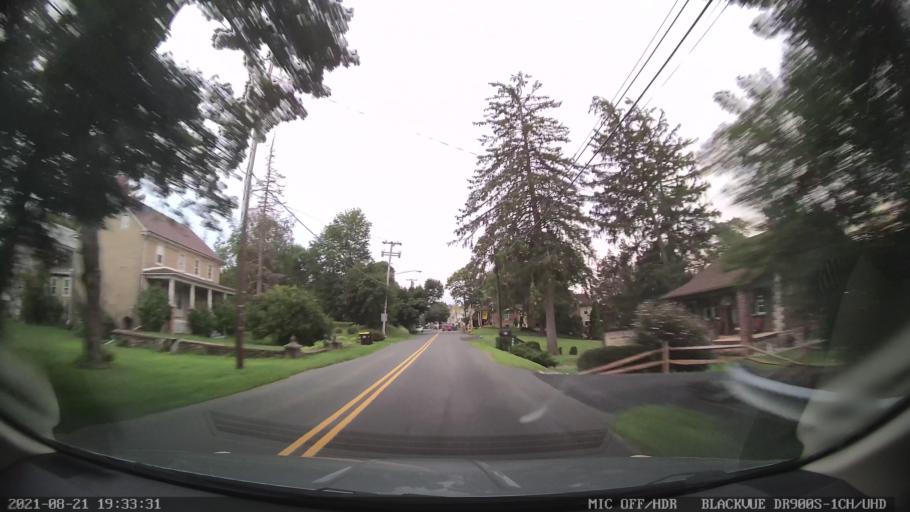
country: US
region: Pennsylvania
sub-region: Berks County
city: Oley
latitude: 40.3920
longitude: -75.7948
